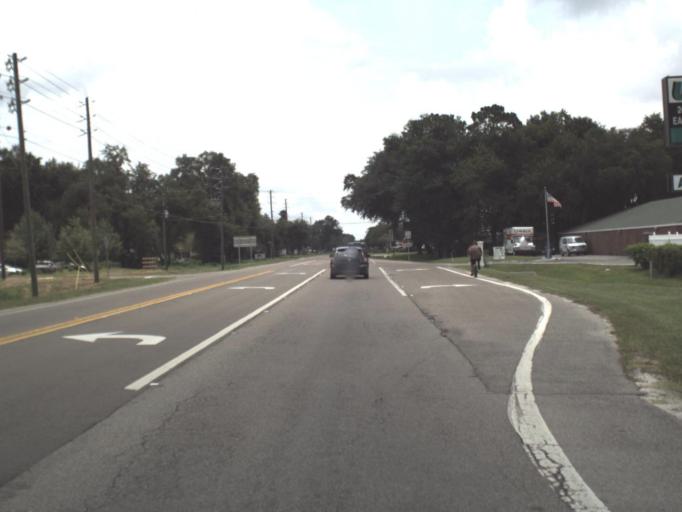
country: US
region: Florida
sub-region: Pasco County
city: Zephyrhills West
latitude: 28.2299
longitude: -82.2111
